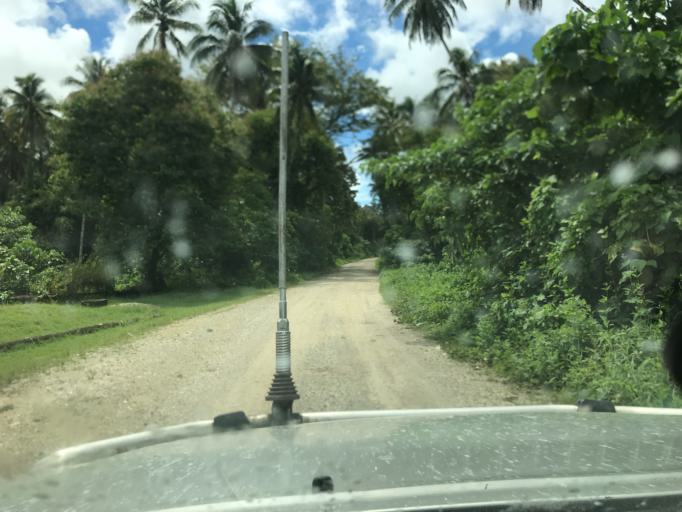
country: SB
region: Malaita
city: Auki
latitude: -8.3803
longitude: 160.7219
